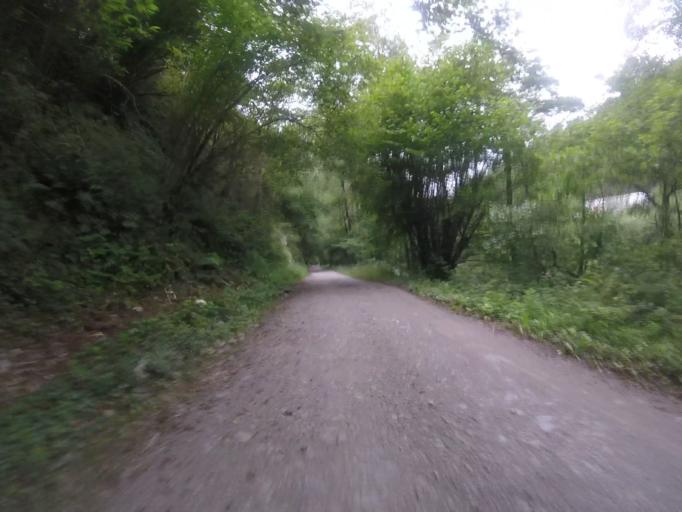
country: ES
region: Navarre
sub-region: Provincia de Navarra
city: Igantzi
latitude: 43.2105
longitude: -1.6692
